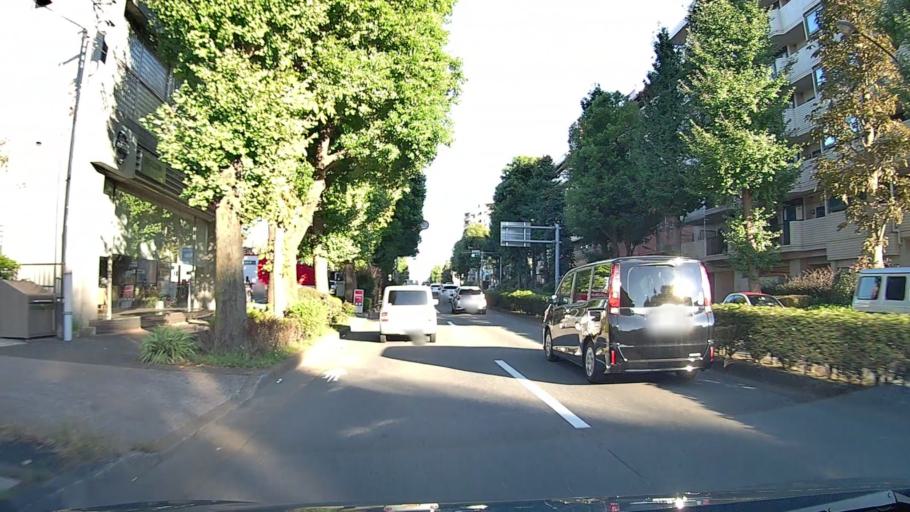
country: JP
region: Saitama
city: Wako
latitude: 35.7580
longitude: 139.5907
